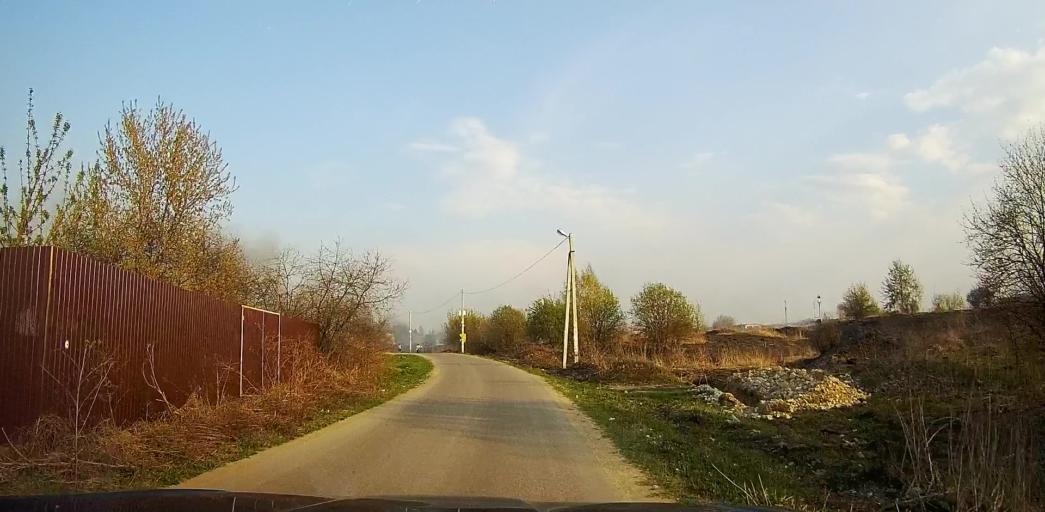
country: RU
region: Moskovskaya
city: Andreyevskoye
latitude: 55.5448
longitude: 37.9709
